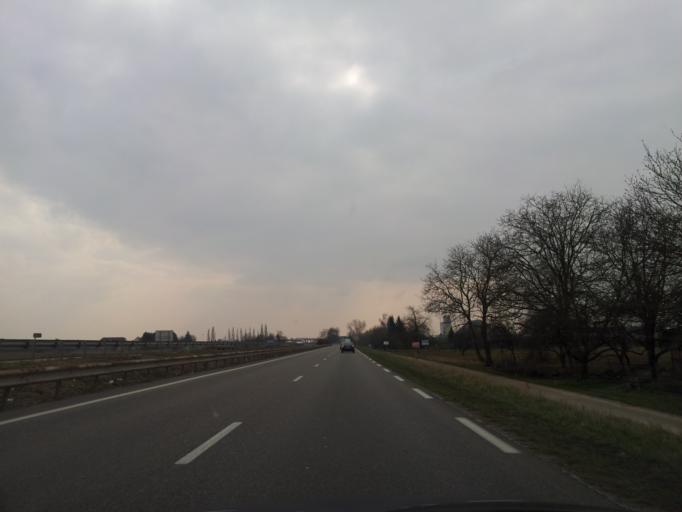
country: FR
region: Alsace
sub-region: Departement du Bas-Rhin
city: Erstein
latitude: 48.4290
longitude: 7.6434
